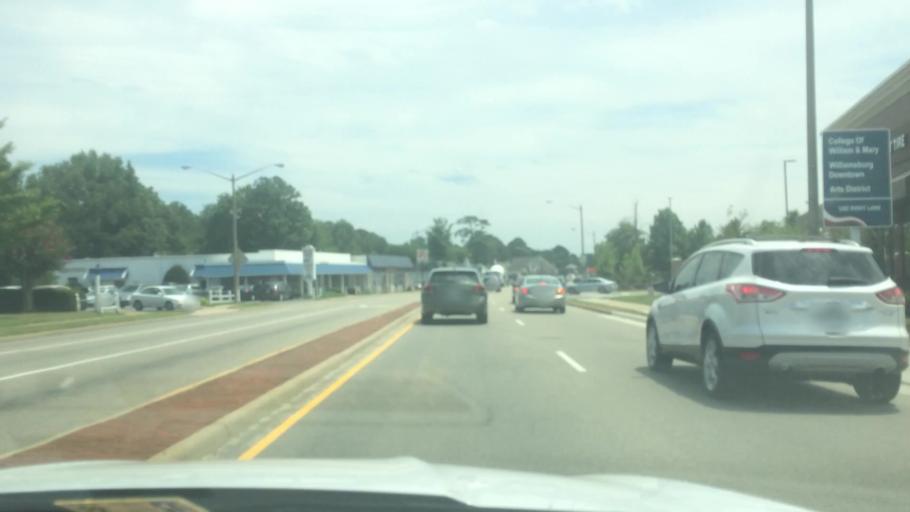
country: US
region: Virginia
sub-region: James City County
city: Williamsburg
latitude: 37.2915
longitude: -76.7236
